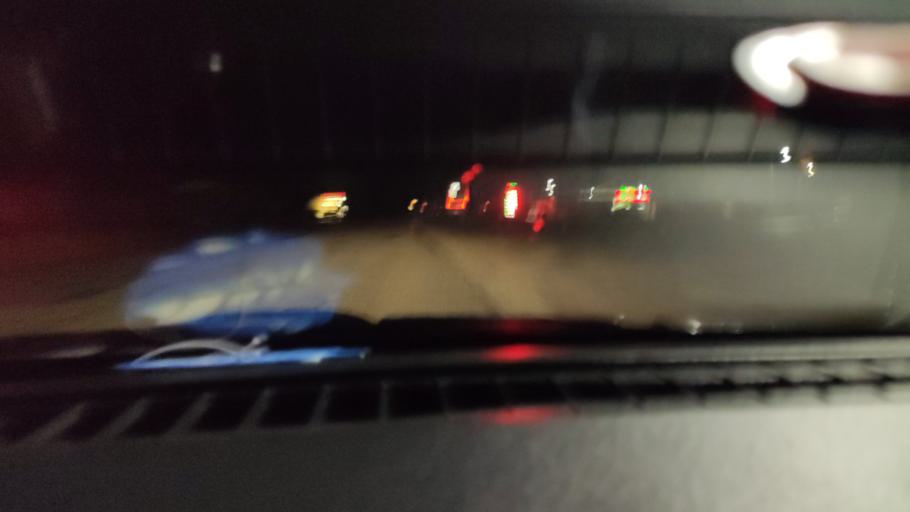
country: RU
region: Udmurtiya
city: Votkinsk
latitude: 57.0305
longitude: 53.9229
